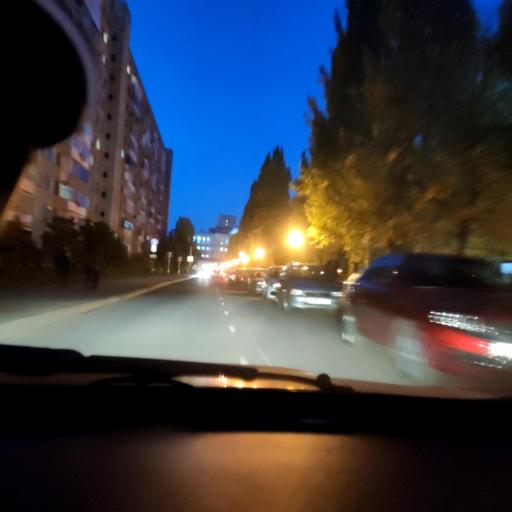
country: RU
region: Samara
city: Tol'yatti
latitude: 53.5308
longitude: 49.3186
